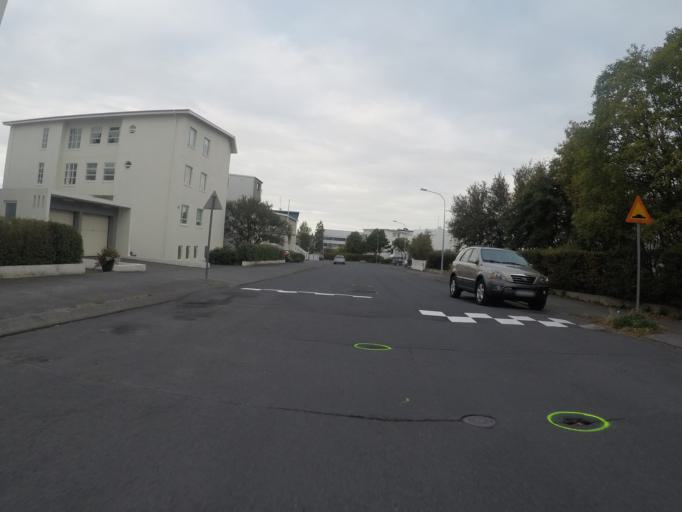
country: IS
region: Capital Region
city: Reykjavik
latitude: 64.1494
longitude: -21.8749
